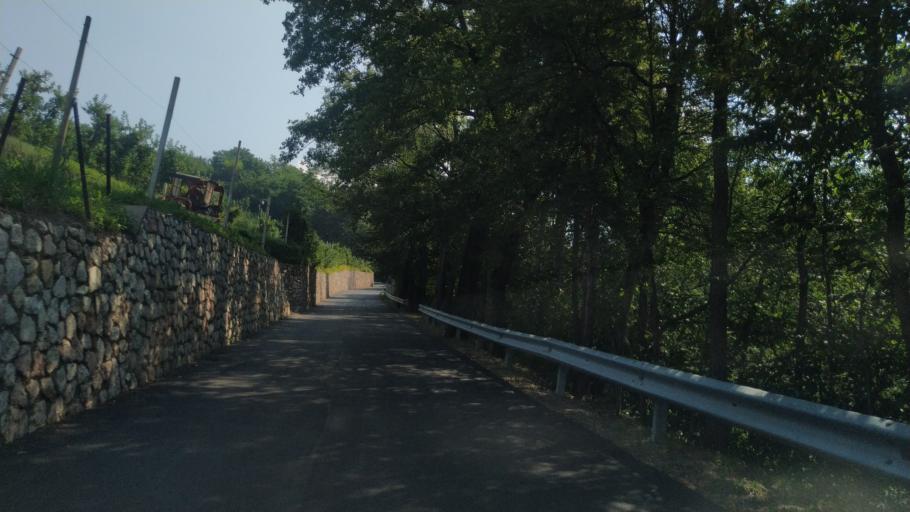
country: IT
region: Trentino-Alto Adige
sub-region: Provincia di Trento
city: Vigo di Ton
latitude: 46.2721
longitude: 11.0700
